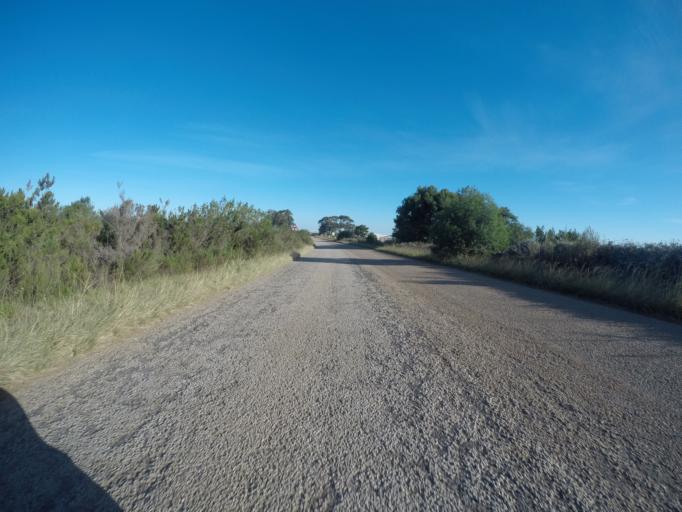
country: ZA
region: Eastern Cape
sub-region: Cacadu District Municipality
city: Kareedouw
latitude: -34.0023
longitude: 24.2343
